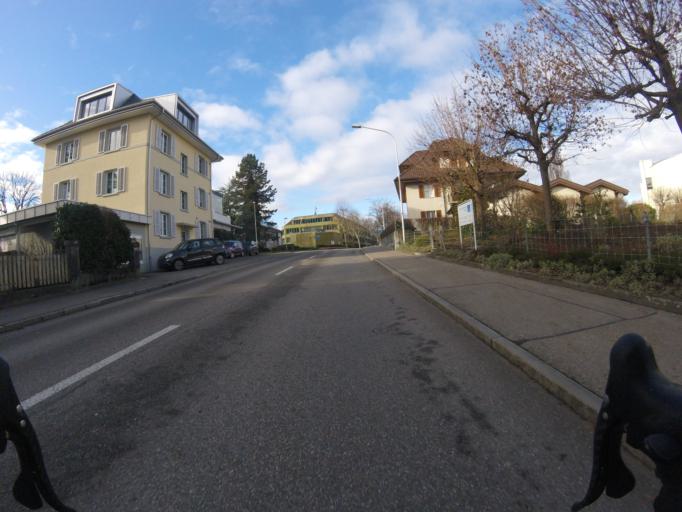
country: CH
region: Bern
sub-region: Bern-Mittelland District
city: Bolligen
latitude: 46.9544
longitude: 7.4882
